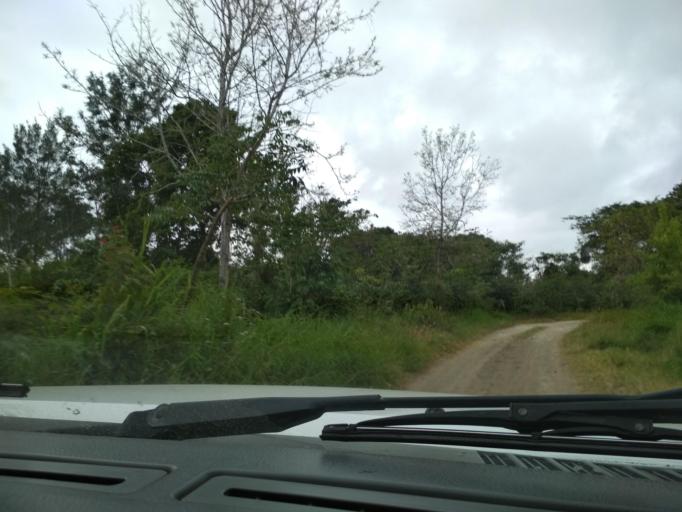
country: MX
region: Veracruz
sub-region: Emiliano Zapata
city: Dos Rios
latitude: 19.5405
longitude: -96.7992
